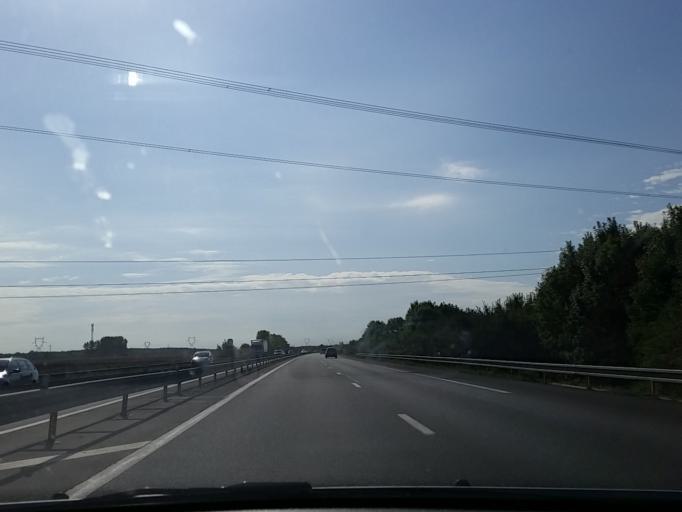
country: FR
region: Centre
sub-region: Departement du Cher
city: Marmagne
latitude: 47.0896
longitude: 2.2541
